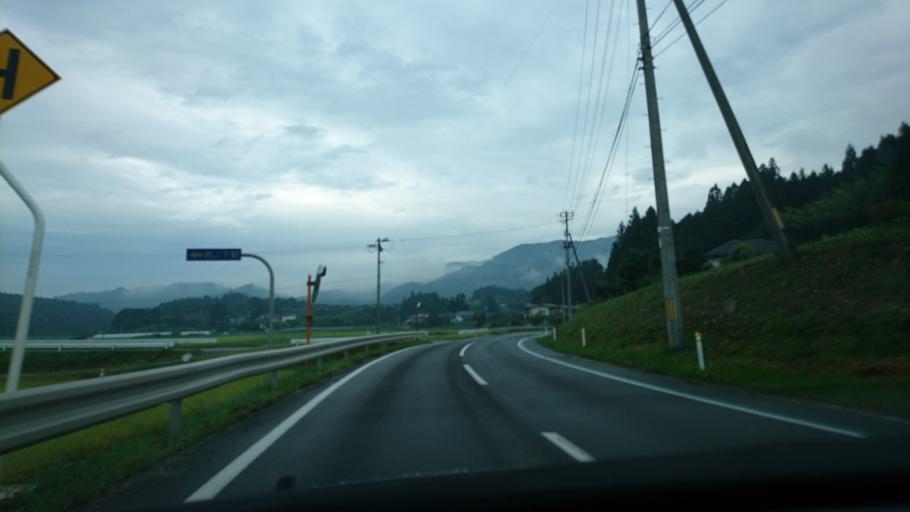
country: JP
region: Iwate
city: Ichinoseki
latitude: 38.9457
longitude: 141.2513
